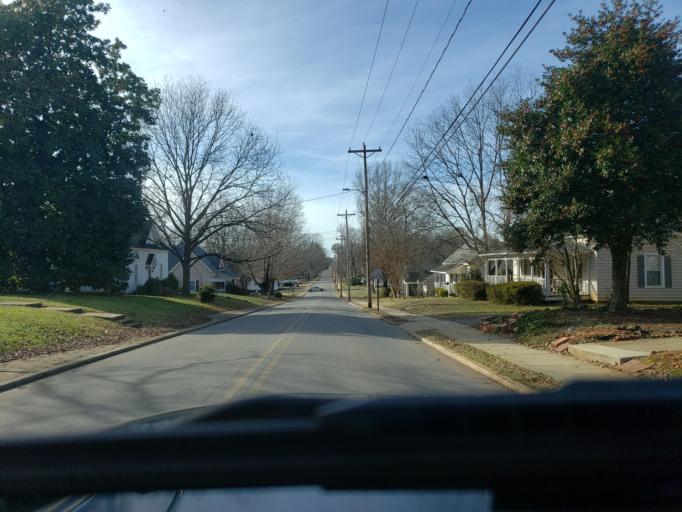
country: US
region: North Carolina
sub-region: Cleveland County
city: Kings Mountain
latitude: 35.2382
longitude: -81.3534
